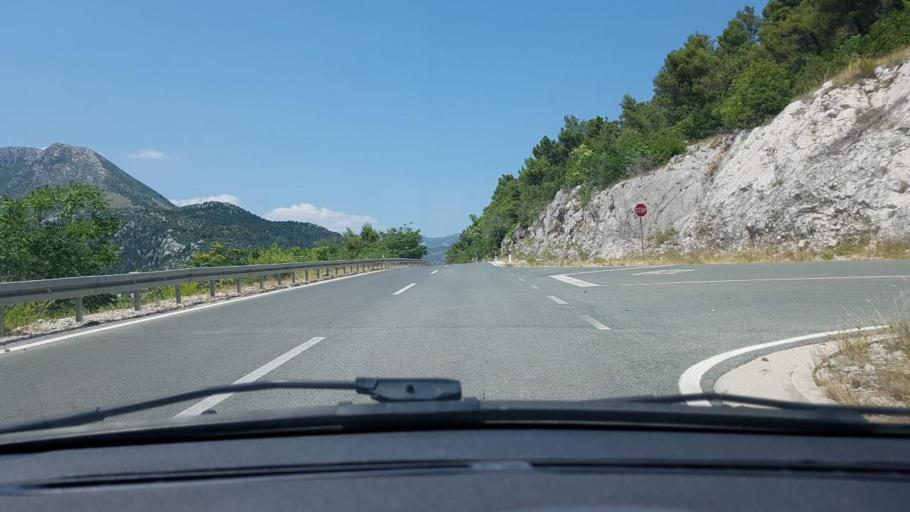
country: HR
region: Splitsko-Dalmatinska
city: Vrgorac
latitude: 43.1960
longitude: 17.3780
